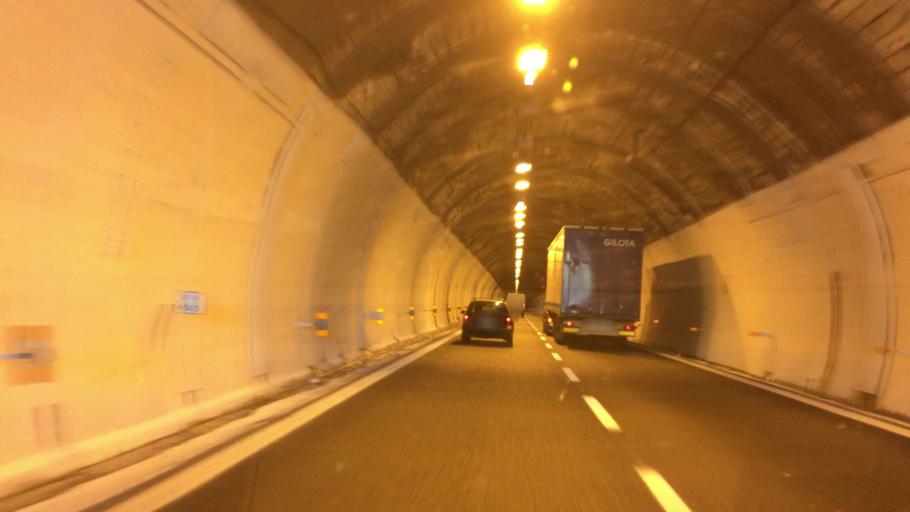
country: IT
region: Liguria
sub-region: Provincia di Genova
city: Sestri Levante
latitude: 44.2913
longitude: 9.3876
